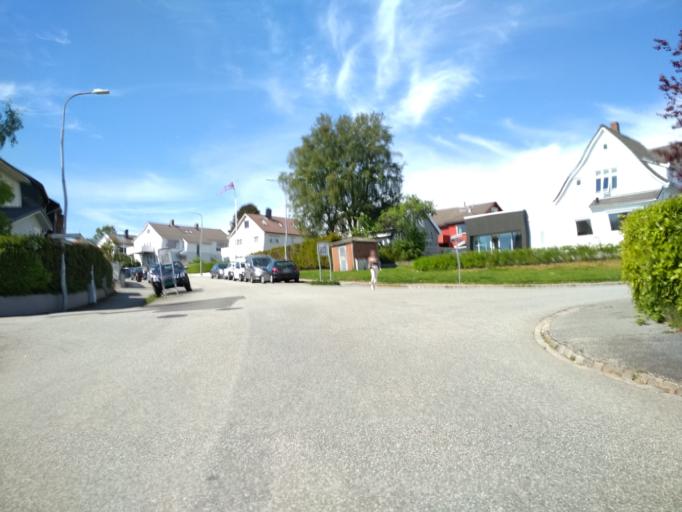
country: NO
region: Rogaland
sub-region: Stavanger
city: Stavanger
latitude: 58.9561
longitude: 5.7333
